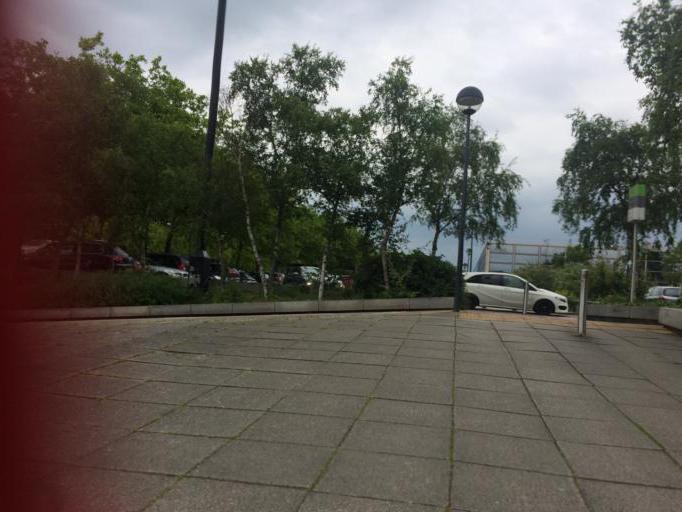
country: GB
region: England
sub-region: Milton Keynes
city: Milton Keynes
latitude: 52.0421
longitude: -0.7608
